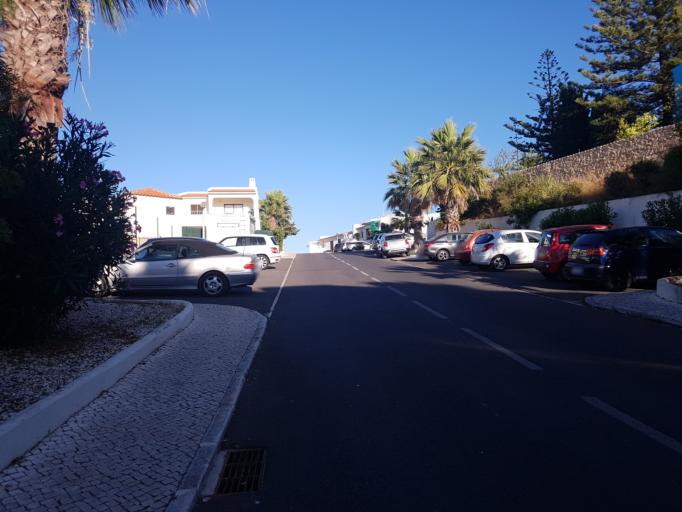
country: PT
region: Faro
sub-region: Lagoa
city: Carvoeiro
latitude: 37.0983
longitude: -8.4683
